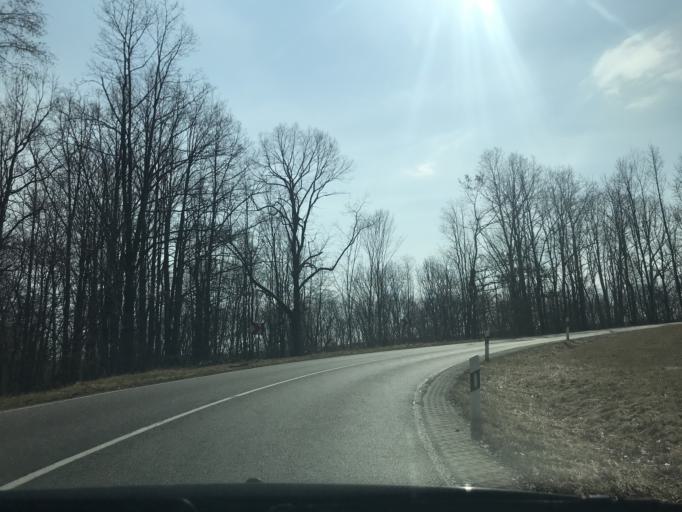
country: DE
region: Saxony
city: Seelitz
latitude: 51.0294
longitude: 12.8009
